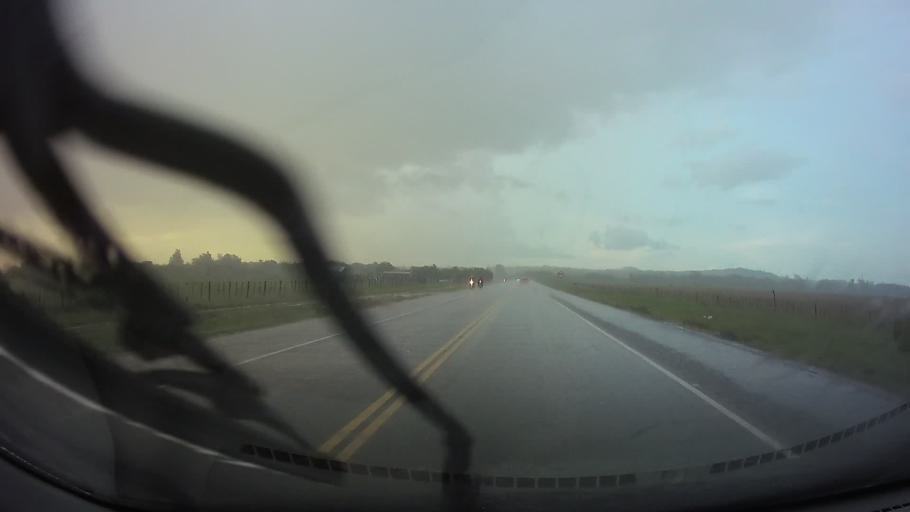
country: PY
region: Paraguari
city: Paraguari
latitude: -25.6334
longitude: -57.1554
